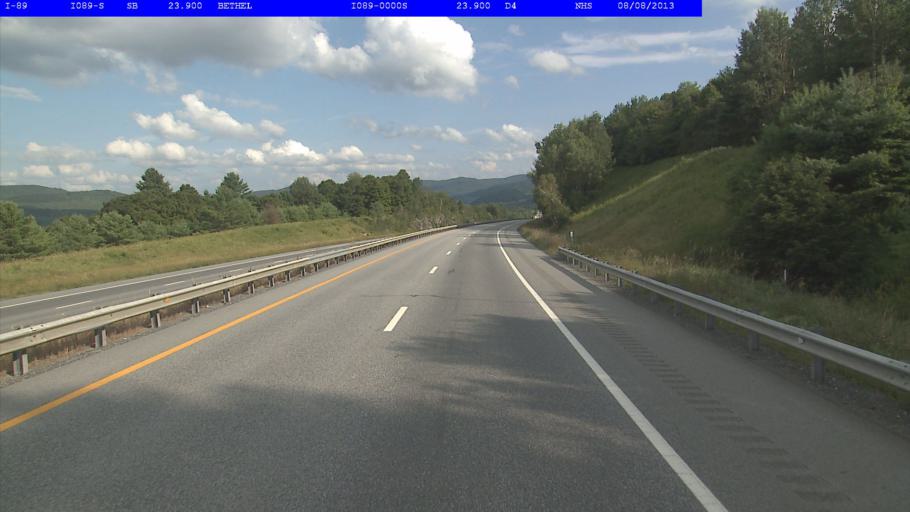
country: US
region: Vermont
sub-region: Orange County
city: Randolph
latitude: 43.8479
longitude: -72.6002
